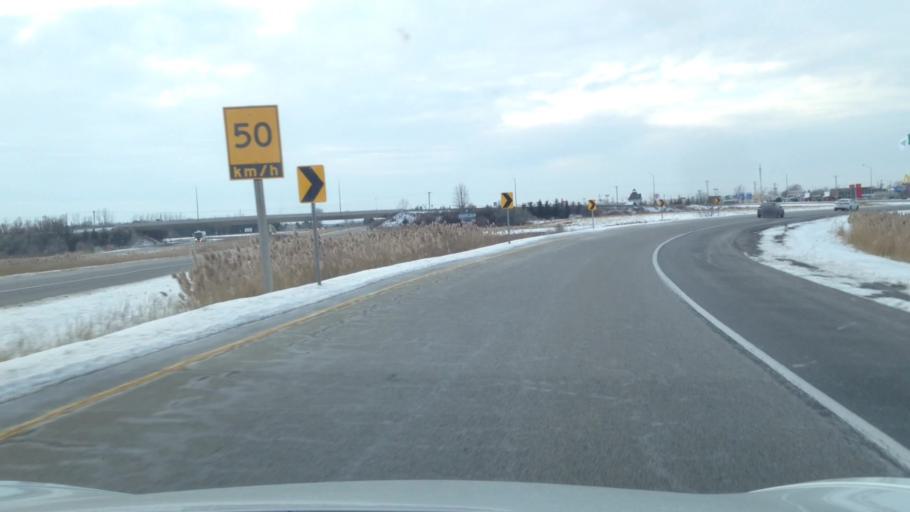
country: CA
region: Ontario
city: Casselman
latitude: 45.3037
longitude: -75.0763
